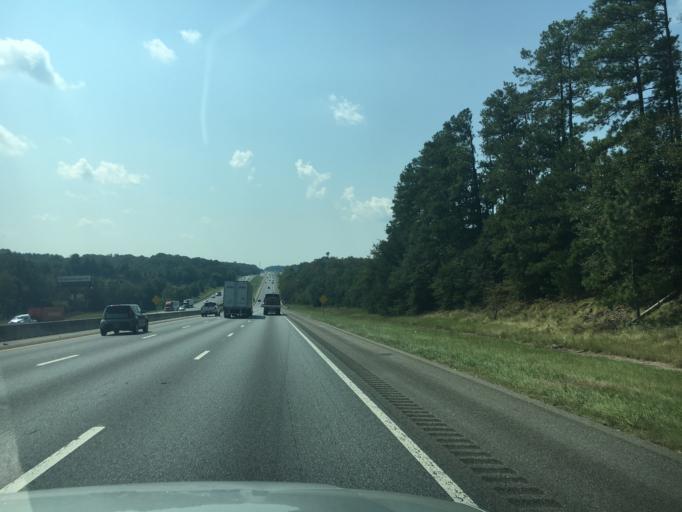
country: US
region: South Carolina
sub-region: Anderson County
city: Piedmont
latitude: 34.7380
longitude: -82.4861
